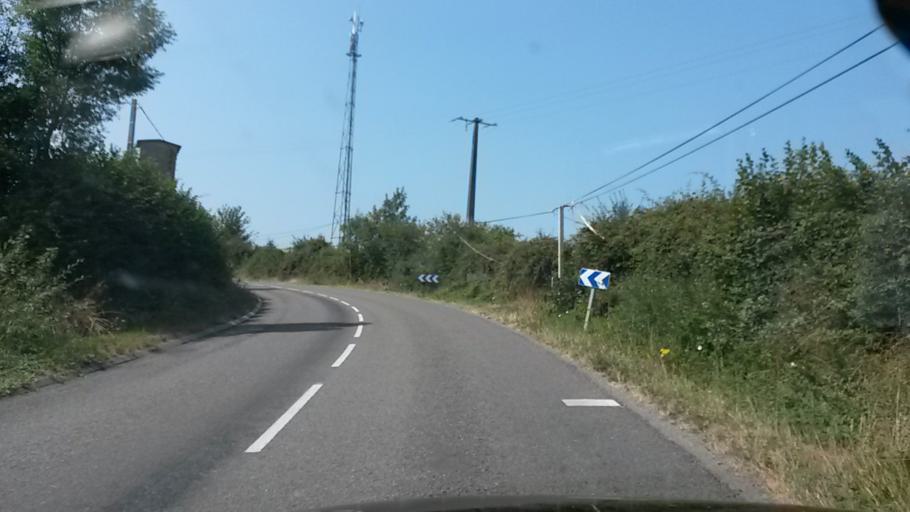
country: FR
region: Pays de la Loire
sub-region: Departement de la Mayenne
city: Saint-Pierre-des-Nids
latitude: 48.4101
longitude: -0.0678
